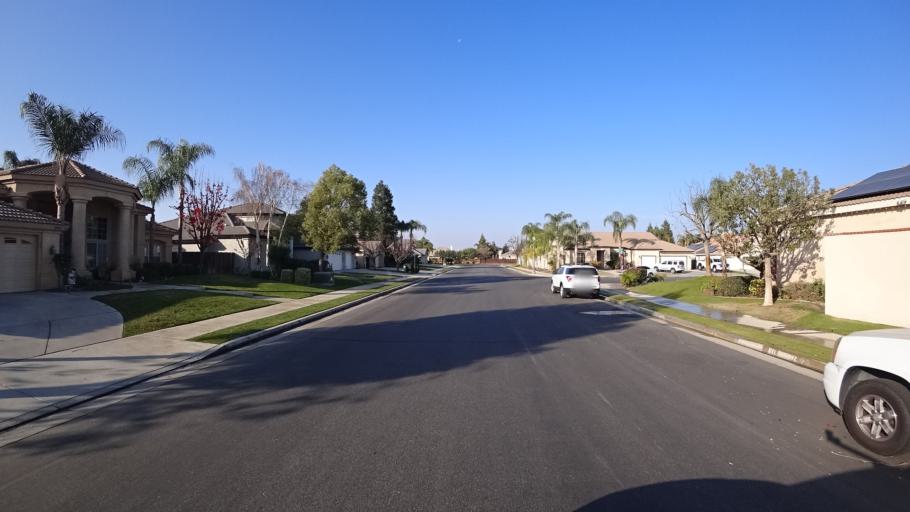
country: US
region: California
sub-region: Kern County
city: Greenacres
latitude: 35.3636
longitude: -119.1235
